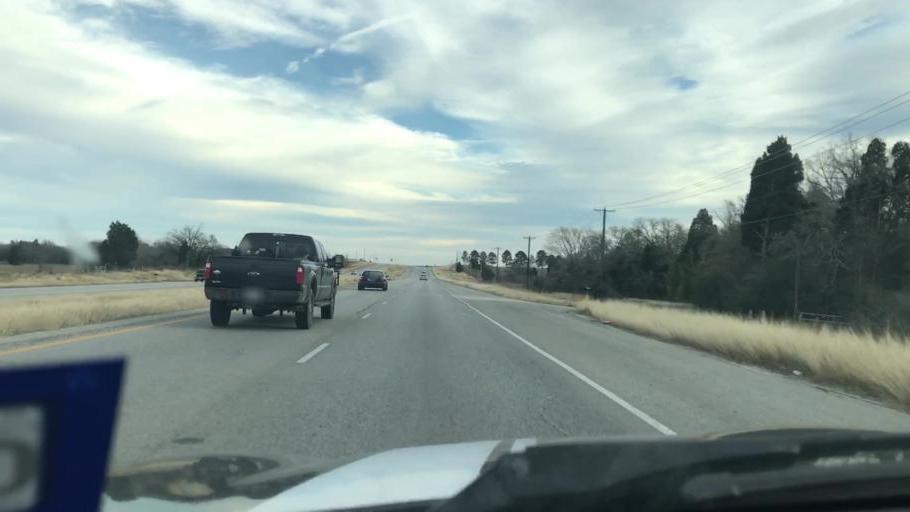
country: US
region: Texas
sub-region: Bastrop County
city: Elgin
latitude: 30.3181
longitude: -97.3146
